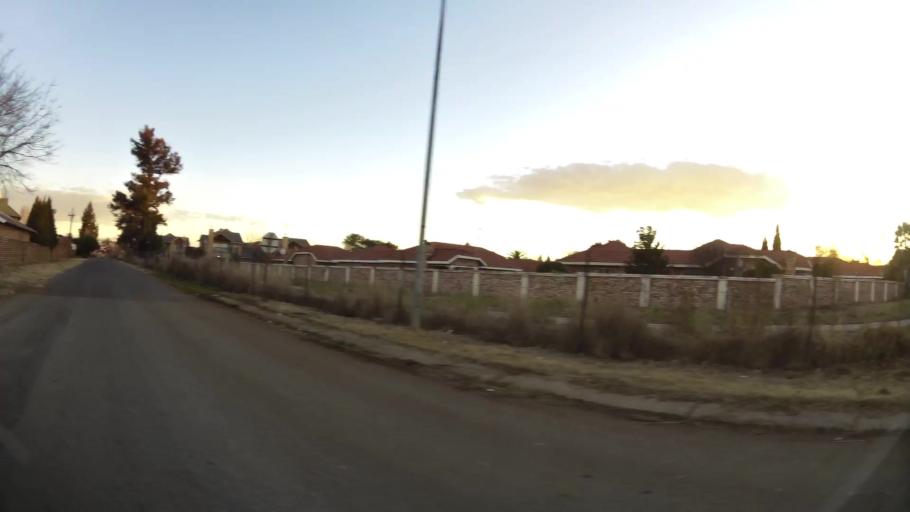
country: ZA
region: North-West
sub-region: Dr Kenneth Kaunda District Municipality
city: Potchefstroom
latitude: -26.7264
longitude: 27.1138
